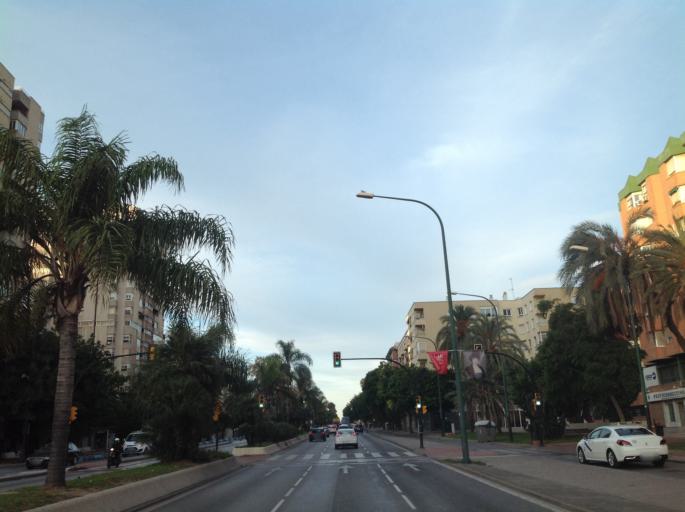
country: ES
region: Andalusia
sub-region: Provincia de Malaga
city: Malaga
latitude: 36.7170
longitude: -4.4381
